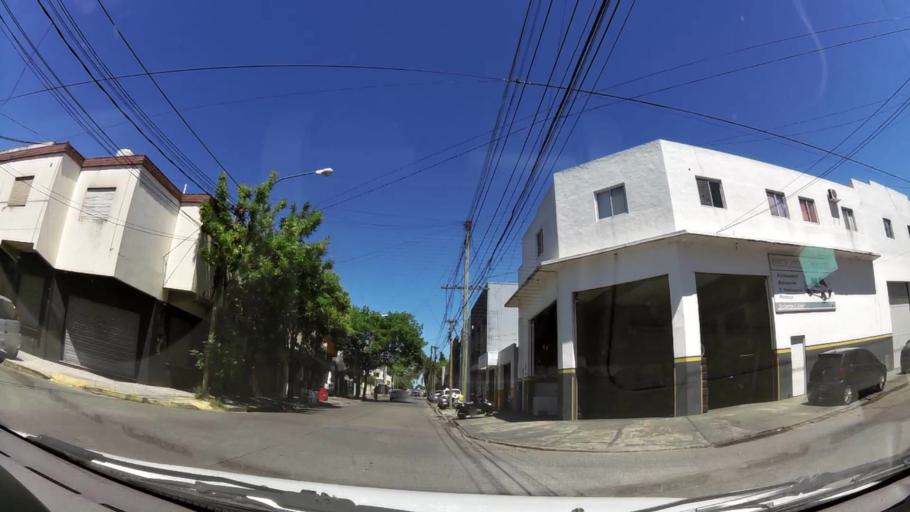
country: AR
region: Buenos Aires
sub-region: Partido de Vicente Lopez
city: Olivos
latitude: -34.5141
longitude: -58.5153
